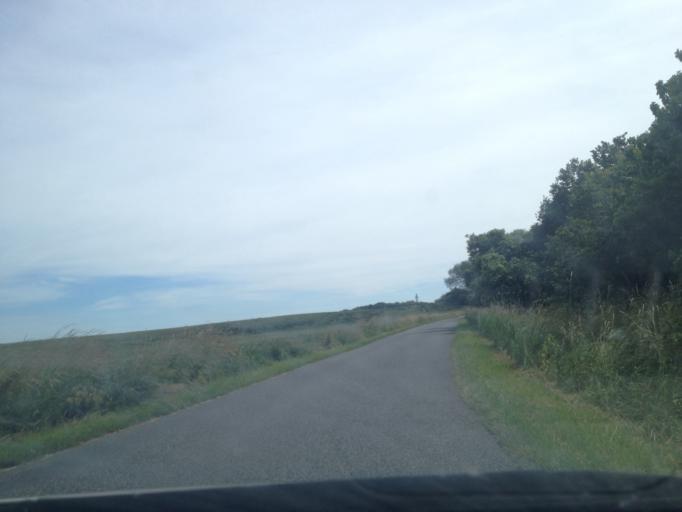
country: DK
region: Central Jutland
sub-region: Samso Kommune
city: Tranebjerg
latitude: 55.7797
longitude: 10.5543
